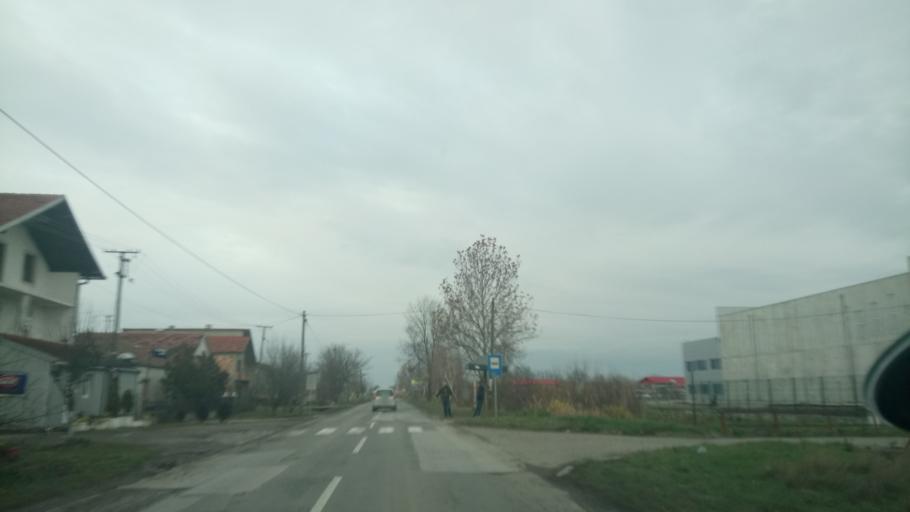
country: RS
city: Vojka
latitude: 44.9523
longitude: 20.1565
